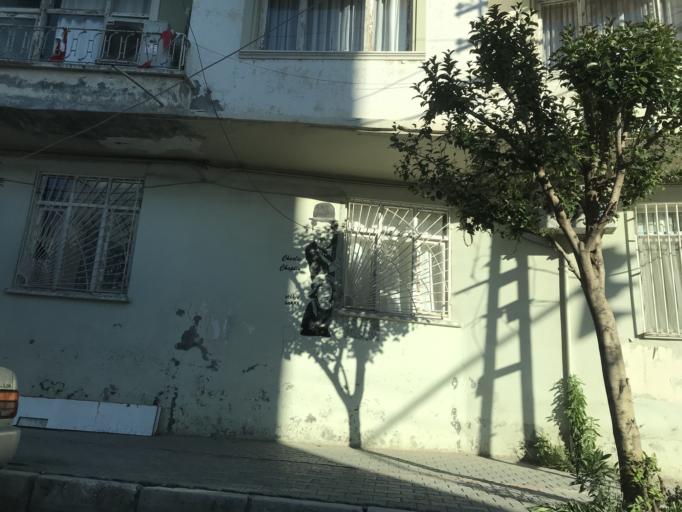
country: TR
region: Hatay
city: Samandag
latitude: 36.0868
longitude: 35.9684
